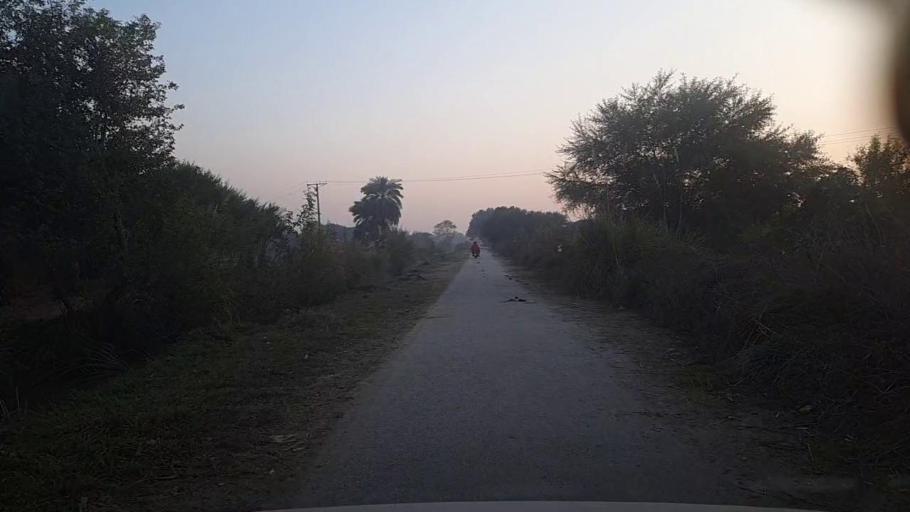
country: PK
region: Sindh
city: Karaundi
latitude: 26.8399
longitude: 68.3699
